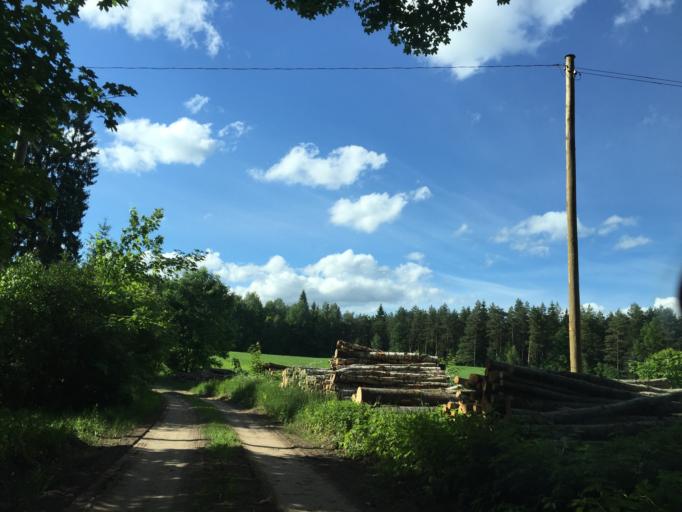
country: LV
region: Vecumnieki
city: Vecumnieki
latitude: 56.4393
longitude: 24.5887
